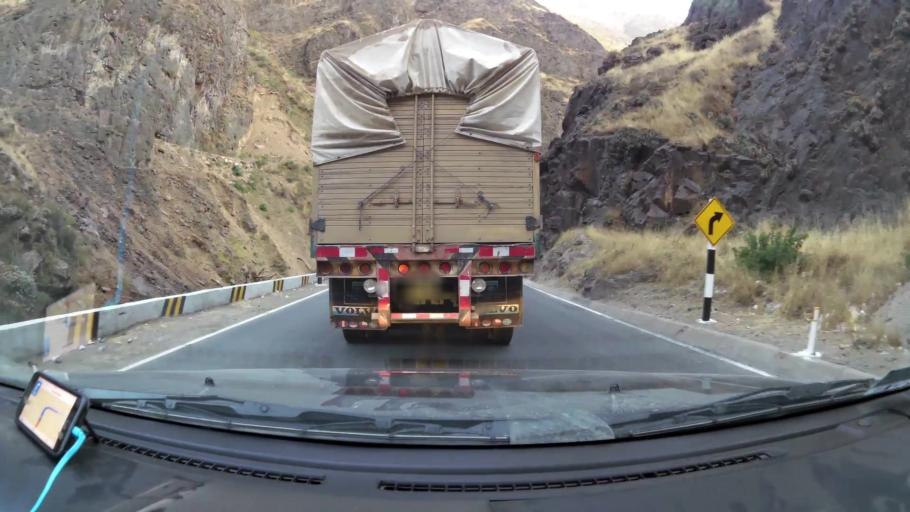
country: PE
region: Lima
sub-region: Provincia de Huarochiri
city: San Mateo
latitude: -11.8080
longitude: -76.3425
